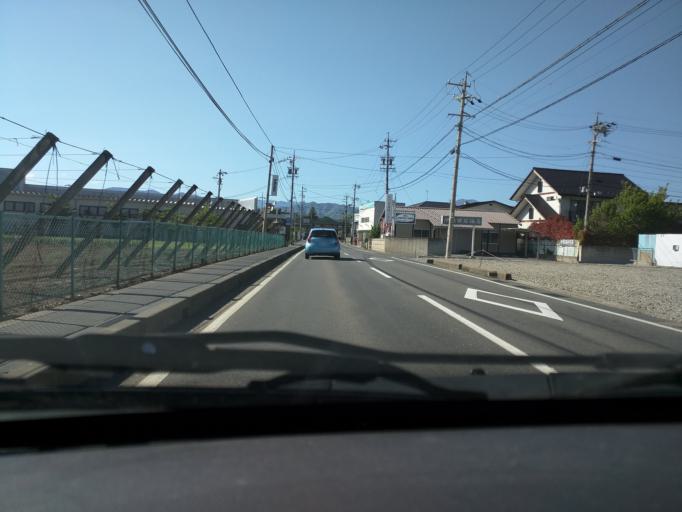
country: JP
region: Nagano
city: Nagano-shi
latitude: 36.5701
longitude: 138.1990
